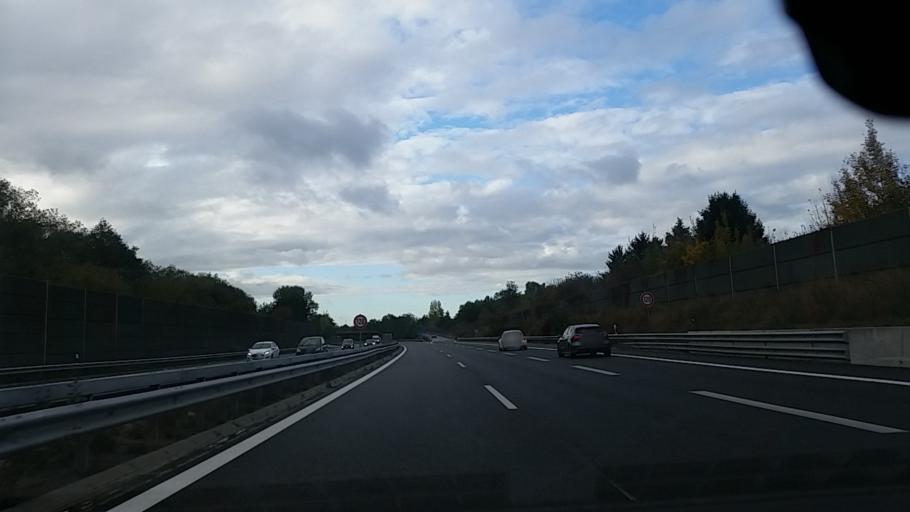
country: DE
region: Hamburg
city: Bergedorf
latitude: 53.4743
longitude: 10.2463
